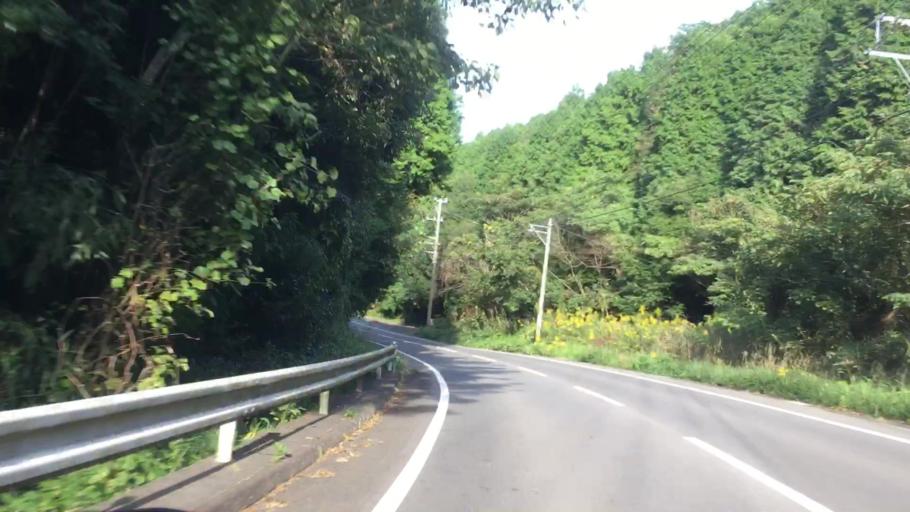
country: JP
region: Nagasaki
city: Sasebo
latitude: 32.9678
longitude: 129.6932
